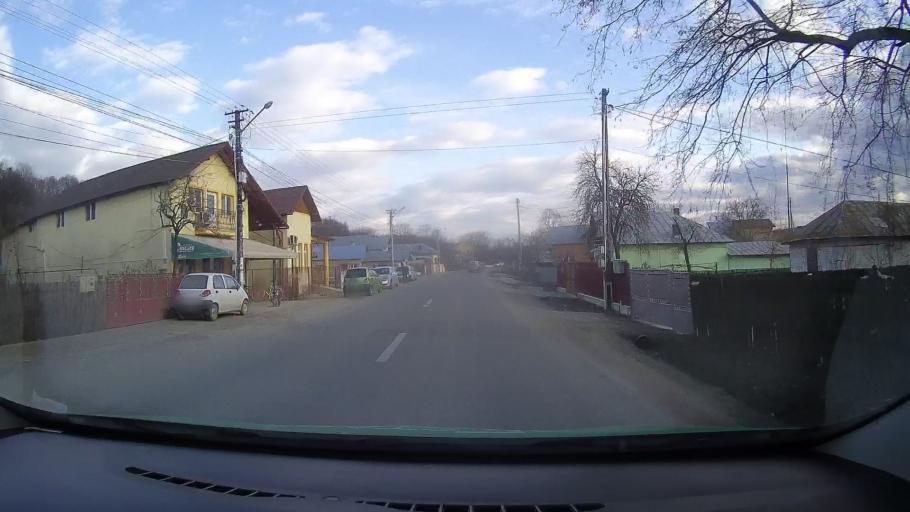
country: RO
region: Dambovita
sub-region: Comuna Gura Ocnitei
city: Gura Ocnitei
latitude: 44.9518
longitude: 25.5559
